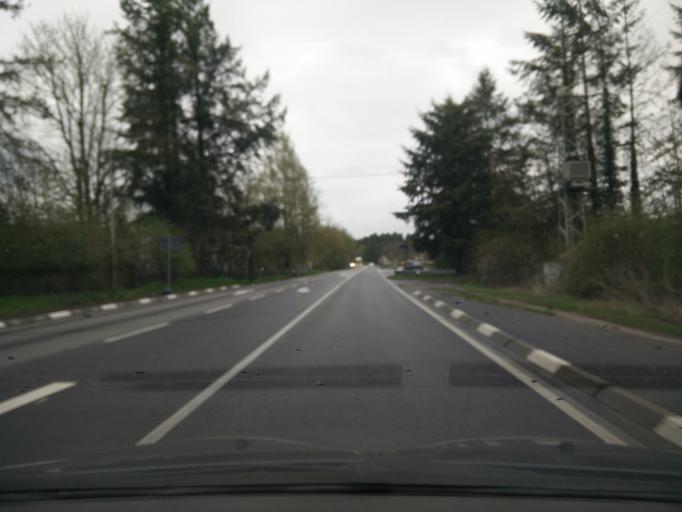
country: DE
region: Rheinland-Pfalz
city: Kandel
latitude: 49.0537
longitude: 8.2012
